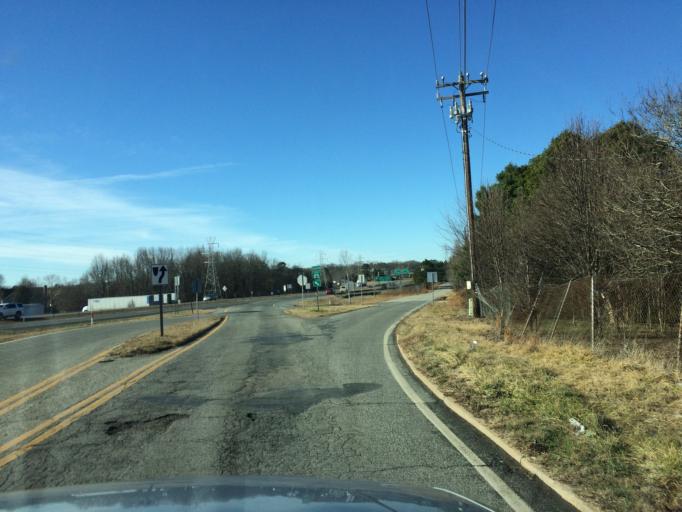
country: US
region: South Carolina
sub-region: Spartanburg County
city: Arcadia
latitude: 34.9706
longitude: -81.9993
